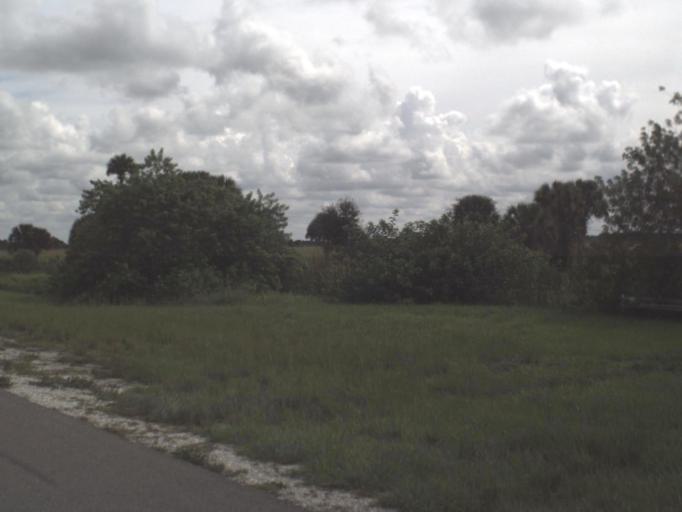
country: US
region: Florida
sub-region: Glades County
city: Buckhead Ridge
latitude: 27.2149
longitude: -81.1107
